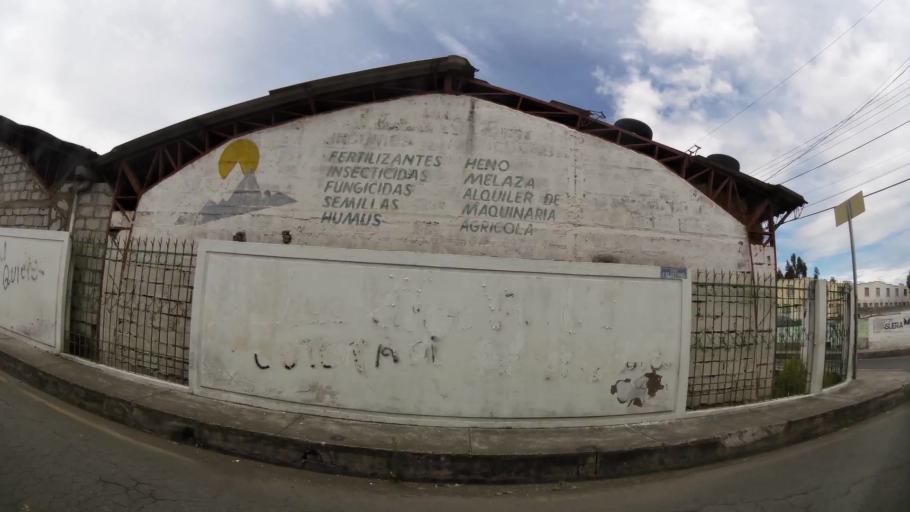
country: EC
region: Cotopaxi
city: San Miguel de Salcedo
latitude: -1.0420
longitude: -78.5922
